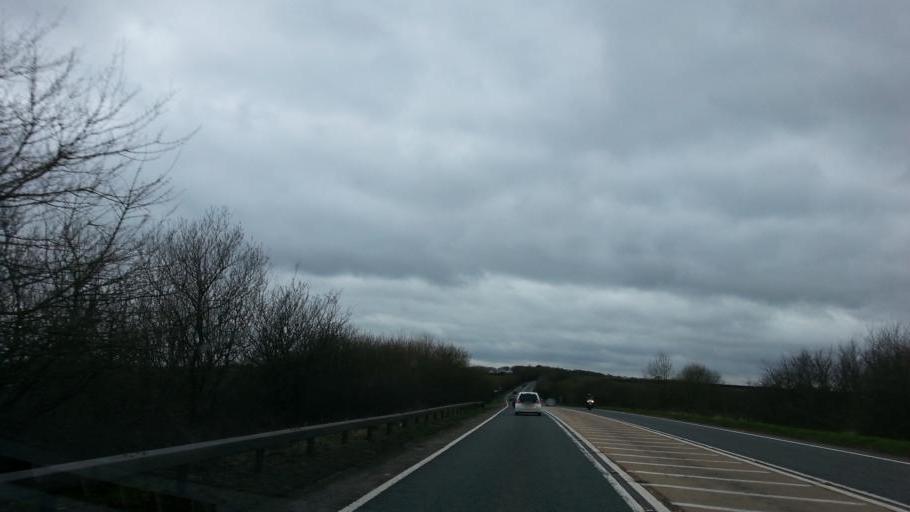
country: GB
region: England
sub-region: Devon
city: Tiverton
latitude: 50.9403
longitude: -3.5674
